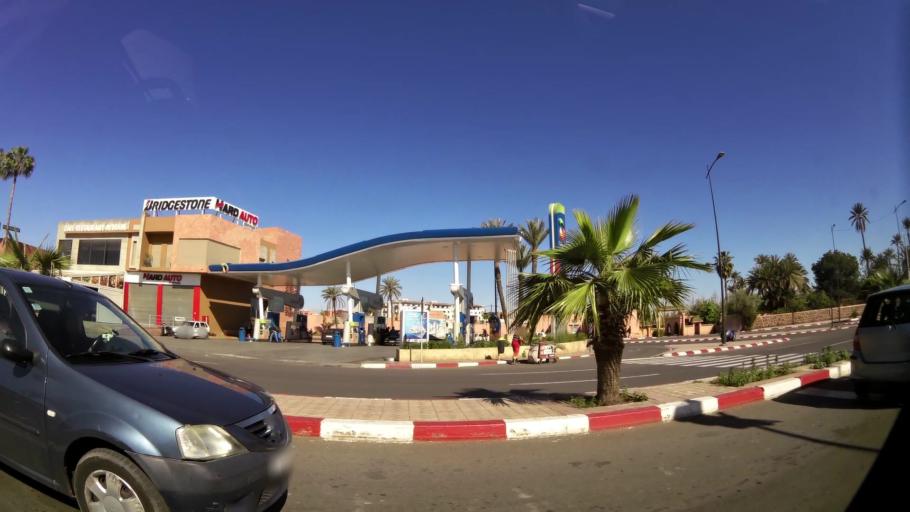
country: MA
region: Marrakech-Tensift-Al Haouz
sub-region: Marrakech
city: Marrakesh
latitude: 31.6413
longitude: -7.9961
